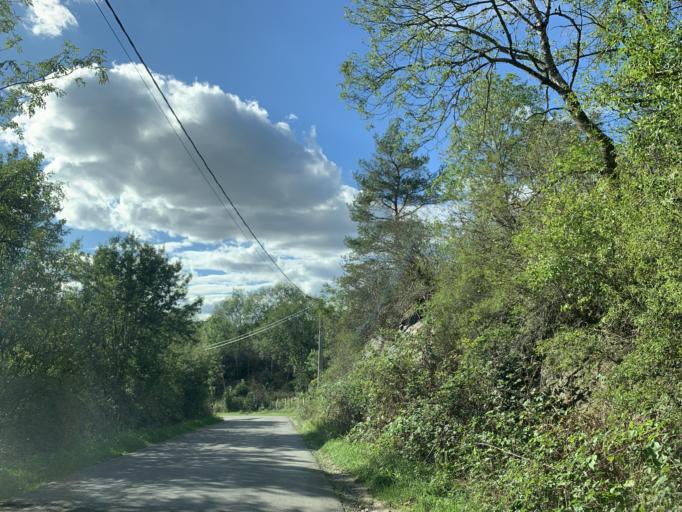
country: BE
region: Wallonia
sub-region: Province du Luxembourg
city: Tellin
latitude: 50.0944
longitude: 5.2779
